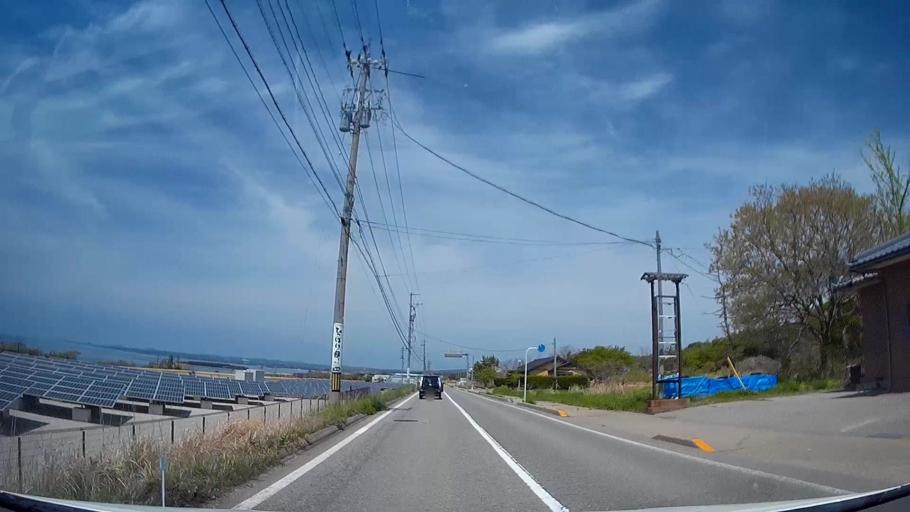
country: JP
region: Ishikawa
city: Hakui
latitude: 36.9340
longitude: 136.7570
